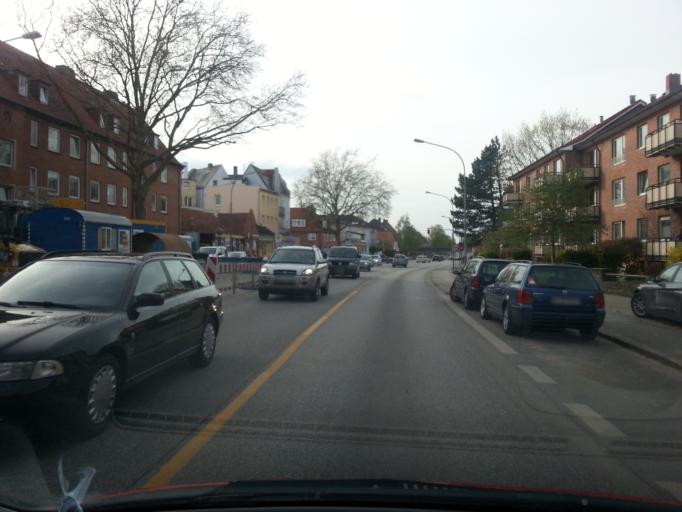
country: DE
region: Schleswig-Holstein
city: Luebeck
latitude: 53.8503
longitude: 10.7041
